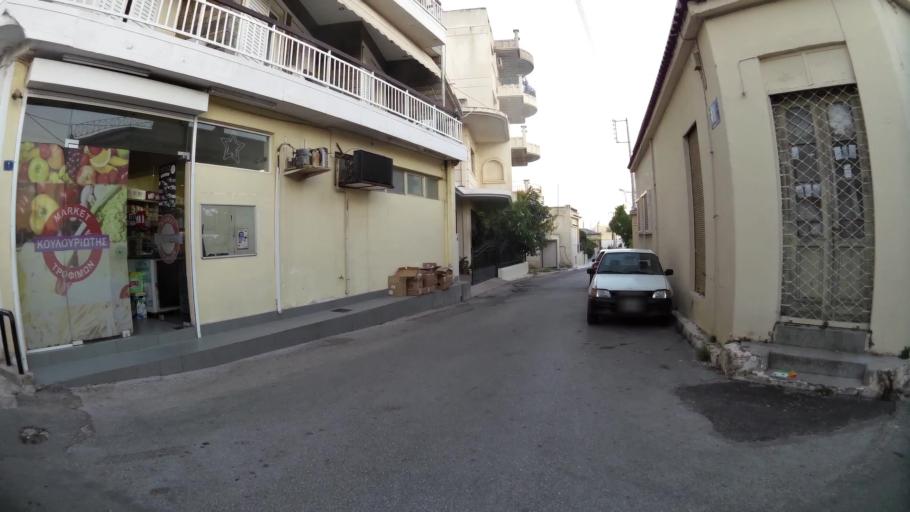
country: GR
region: Attica
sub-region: Nomarchia Anatolikis Attikis
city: Spata
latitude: 37.9641
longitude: 23.9163
